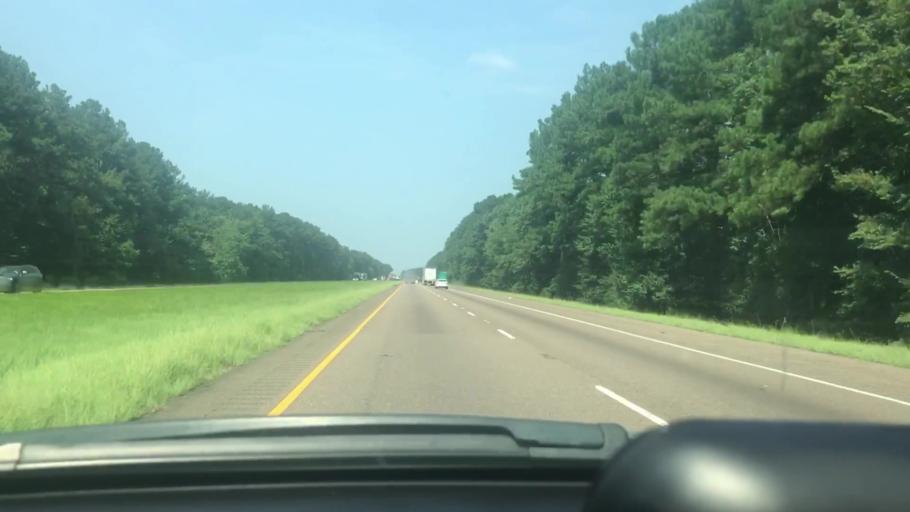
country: US
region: Louisiana
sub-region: Livingston Parish
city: Livingston
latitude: 30.4742
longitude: -90.7721
